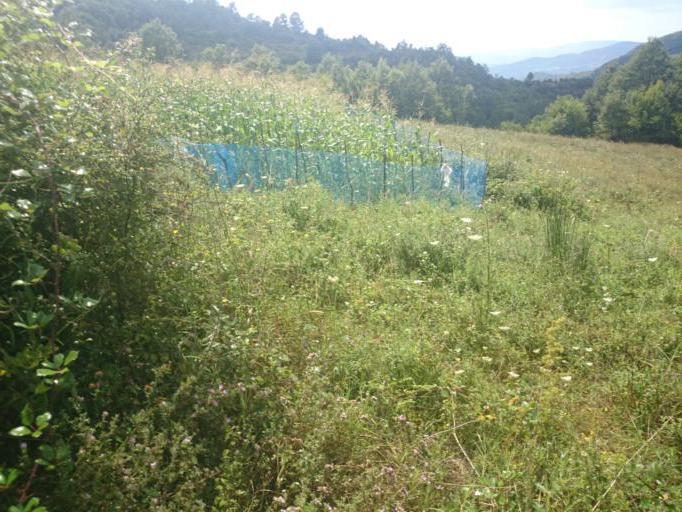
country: AL
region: Elbasan
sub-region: Rrethi i Elbasanit
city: Zavaline
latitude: 40.9509
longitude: 20.2353
